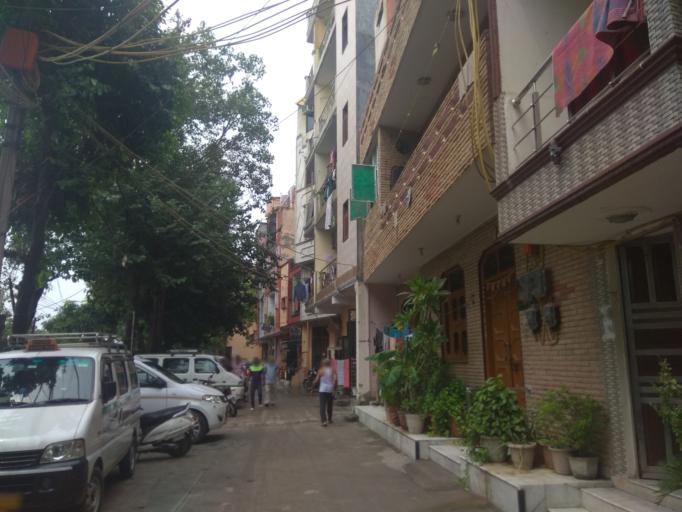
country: IN
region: NCT
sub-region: New Delhi
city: New Delhi
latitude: 28.5751
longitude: 77.2550
